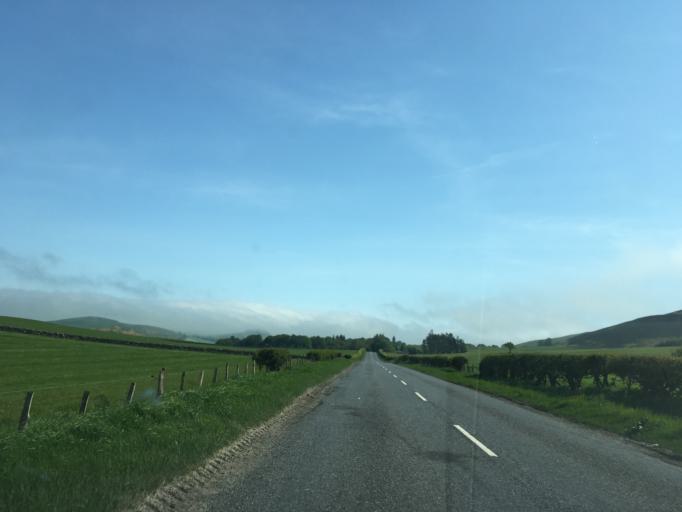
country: GB
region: Scotland
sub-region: The Scottish Borders
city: West Linton
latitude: 55.6755
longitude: -3.4096
